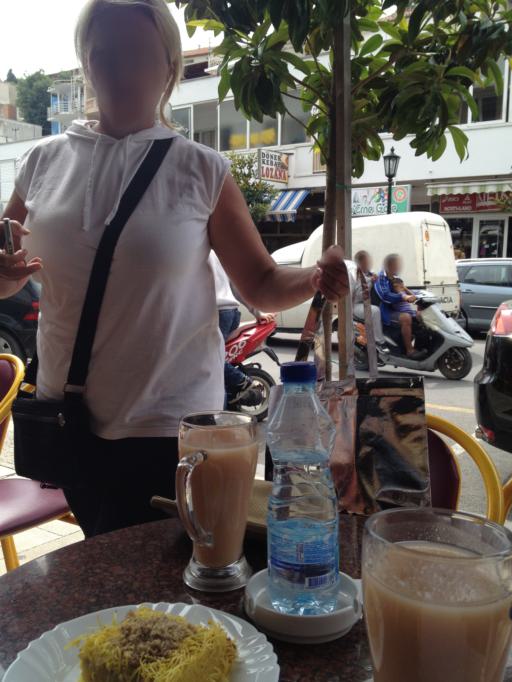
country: ME
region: Ulcinj
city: Ulcinj
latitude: 41.9290
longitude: 19.2065
